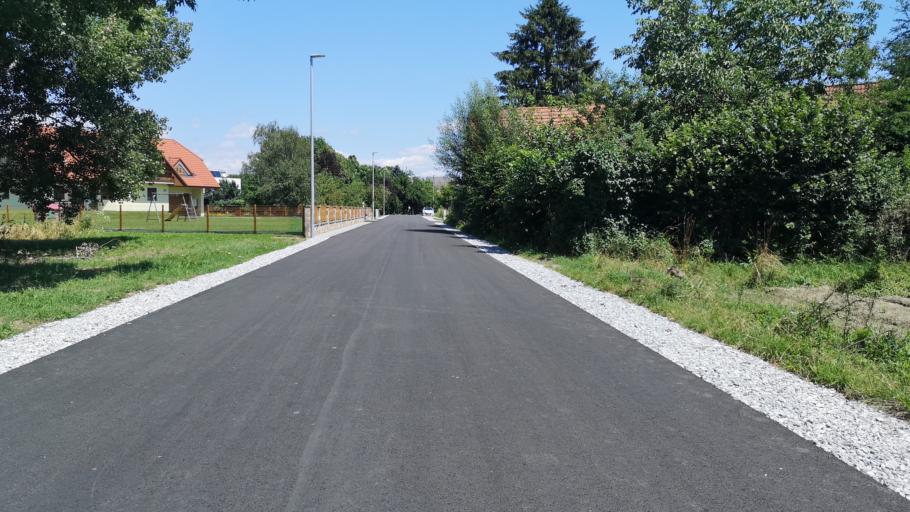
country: AT
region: Styria
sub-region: Politischer Bezirk Graz-Umgebung
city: Feldkirchen bei Graz
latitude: 47.0264
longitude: 15.4613
